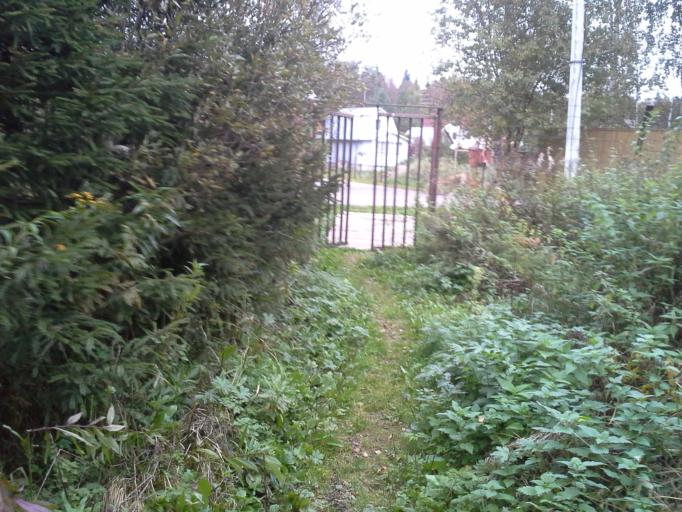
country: RU
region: Moskovskaya
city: Krasnoznamensk
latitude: 55.6174
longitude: 37.0691
